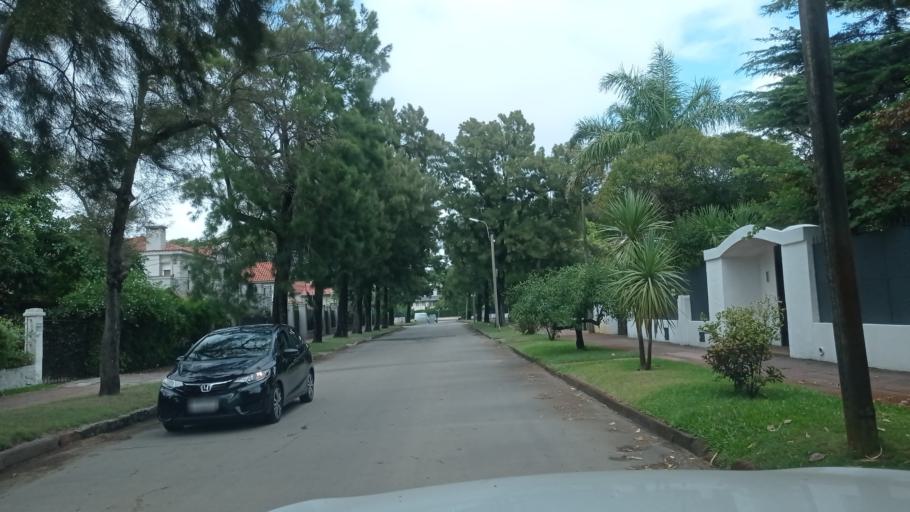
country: UY
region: Canelones
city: Barra de Carrasco
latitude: -34.8879
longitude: -56.0520
